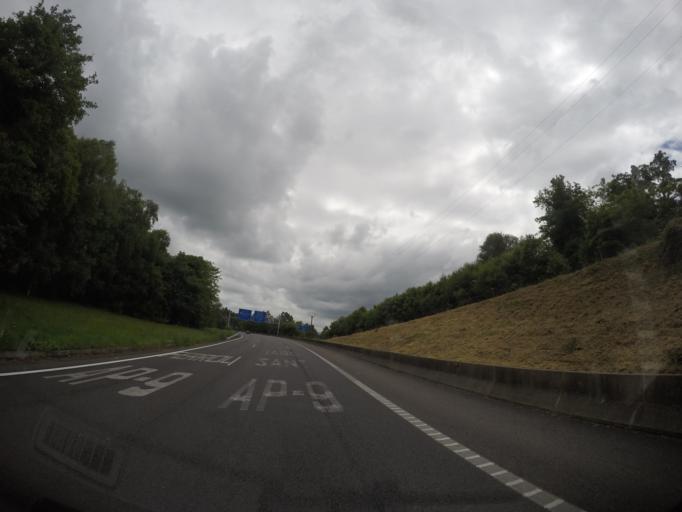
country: ES
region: Galicia
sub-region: Provincia da Coruna
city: Oleiros
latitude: 43.2891
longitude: -8.2939
